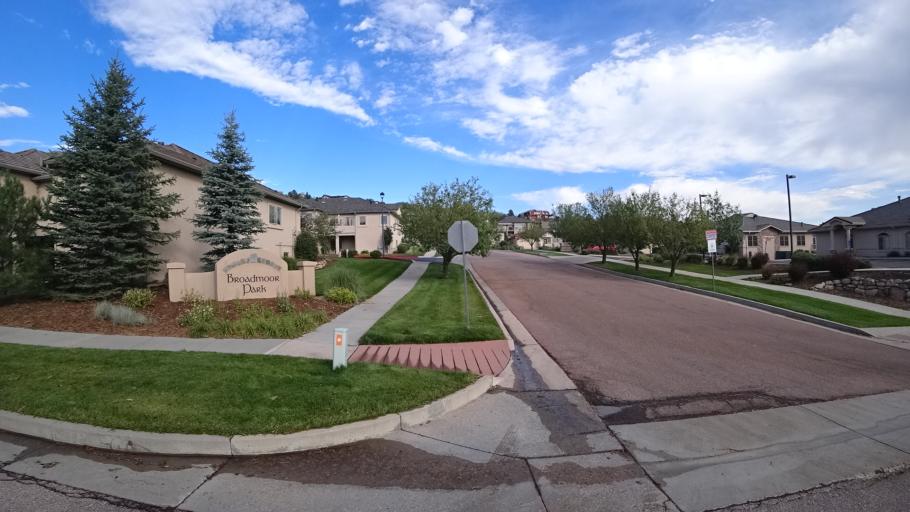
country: US
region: Colorado
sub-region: El Paso County
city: Stratmoor
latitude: 38.7653
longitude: -104.8181
